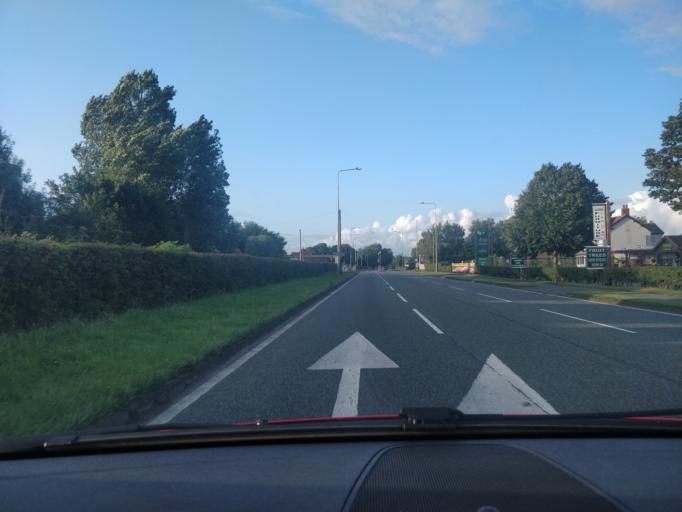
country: GB
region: England
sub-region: Lancashire
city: Tarleton
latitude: 53.6946
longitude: -2.8128
